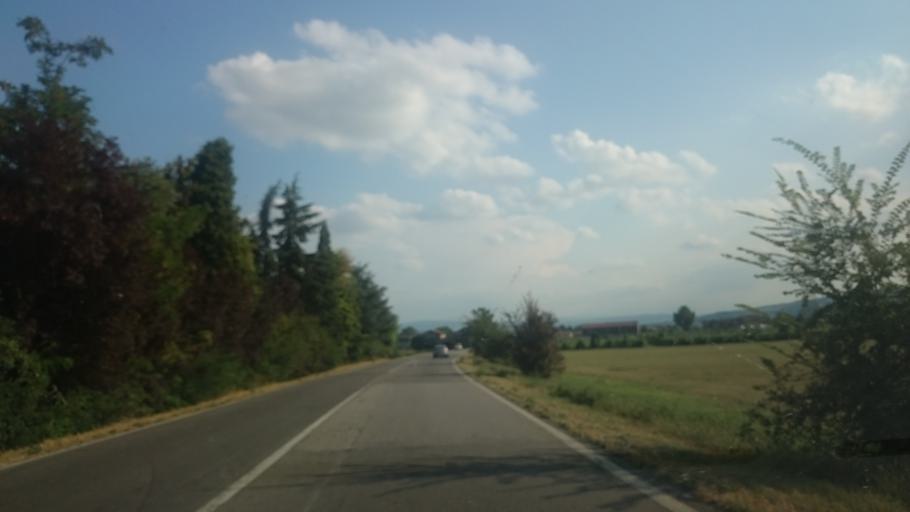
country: IT
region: Emilia-Romagna
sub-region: Provincia di Reggio Emilia
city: Salvaterra
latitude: 44.6127
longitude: 10.7785
